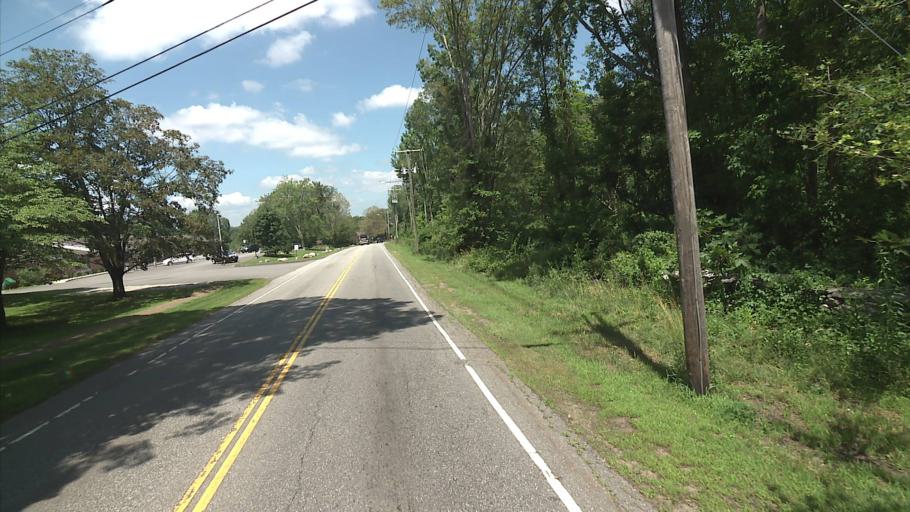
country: US
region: Connecticut
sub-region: Windham County
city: Windham
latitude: 41.7014
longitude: -72.1597
